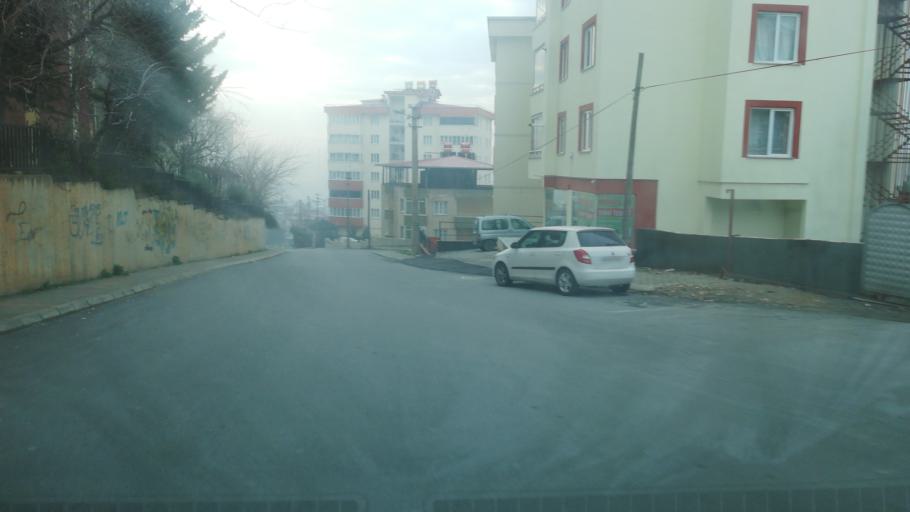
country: TR
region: Kahramanmaras
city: Kahramanmaras
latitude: 37.5940
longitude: 36.9005
